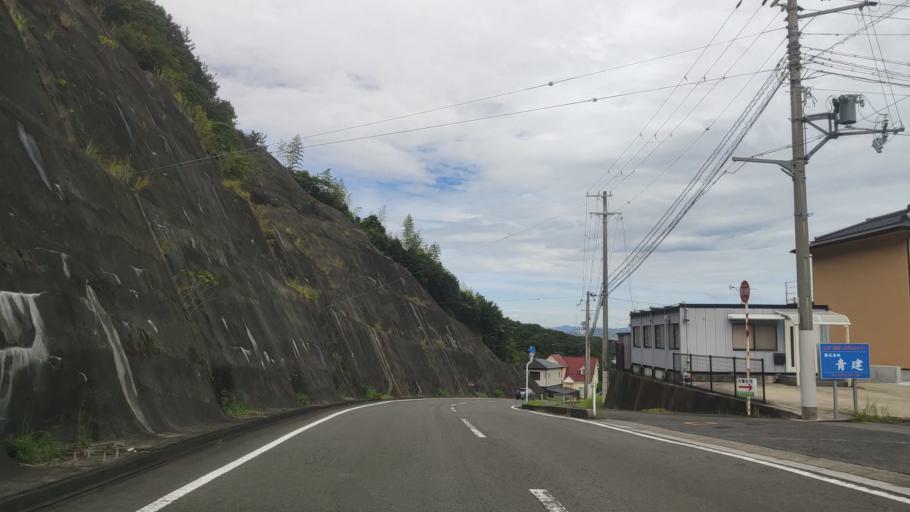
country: JP
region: Wakayama
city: Tanabe
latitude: 33.6881
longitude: 135.3885
